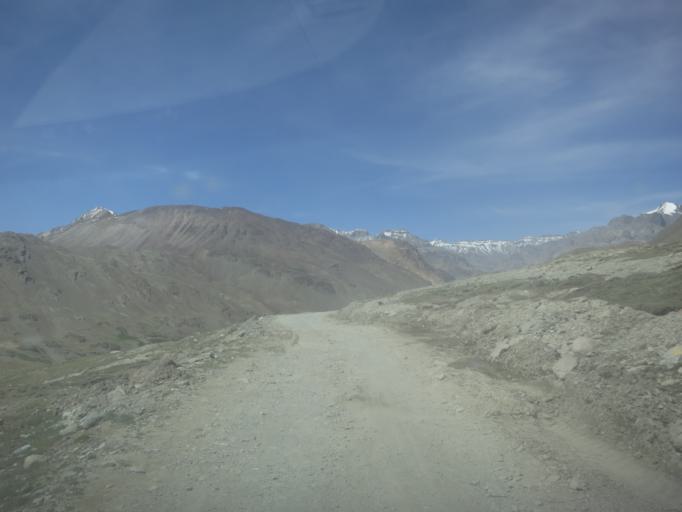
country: IN
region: Himachal Pradesh
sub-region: Kulu
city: Manali
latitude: 32.3992
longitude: 77.6370
